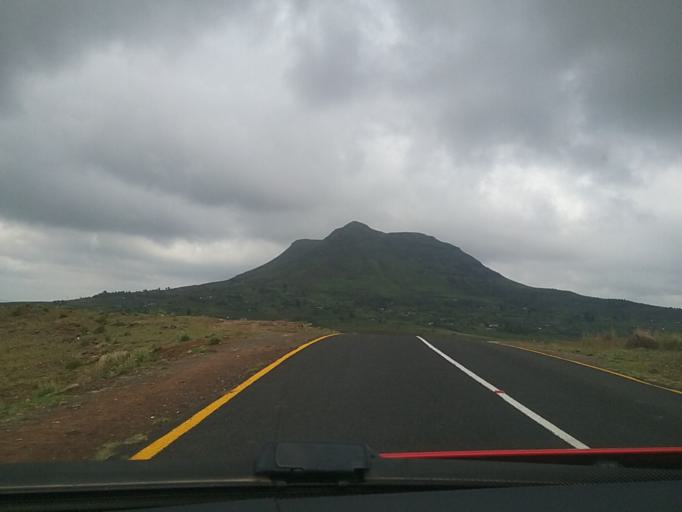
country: LS
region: Berea
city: Teyateyaneng
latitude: -29.2448
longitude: 27.8539
